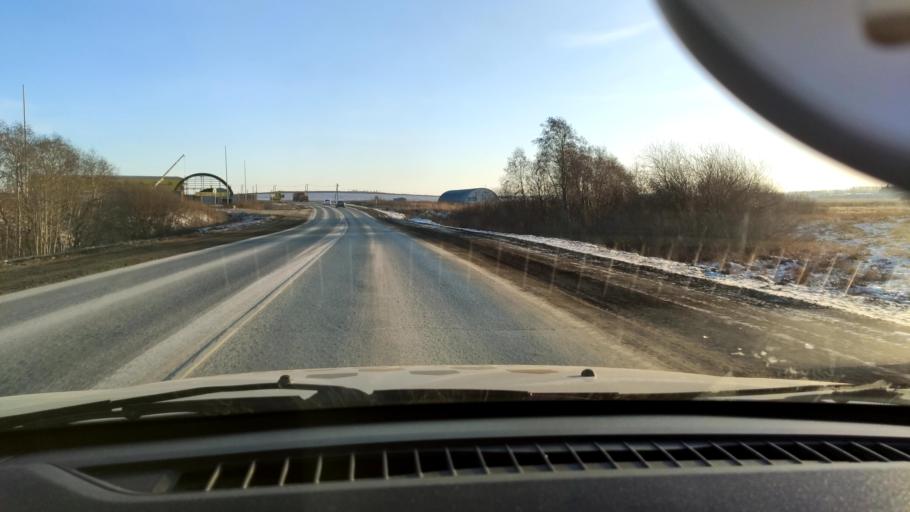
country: RU
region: Perm
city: Froly
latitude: 57.9060
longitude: 56.1988
